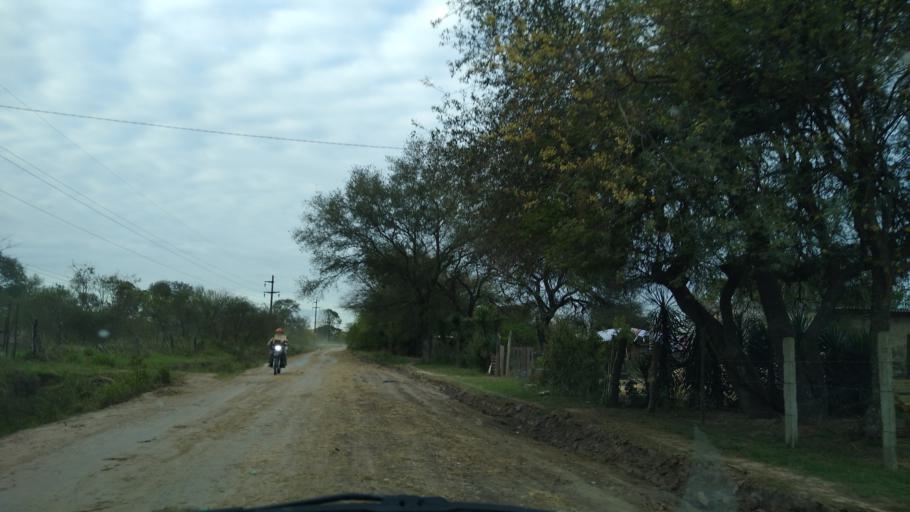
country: AR
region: Chaco
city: Fontana
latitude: -27.3823
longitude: -59.0408
